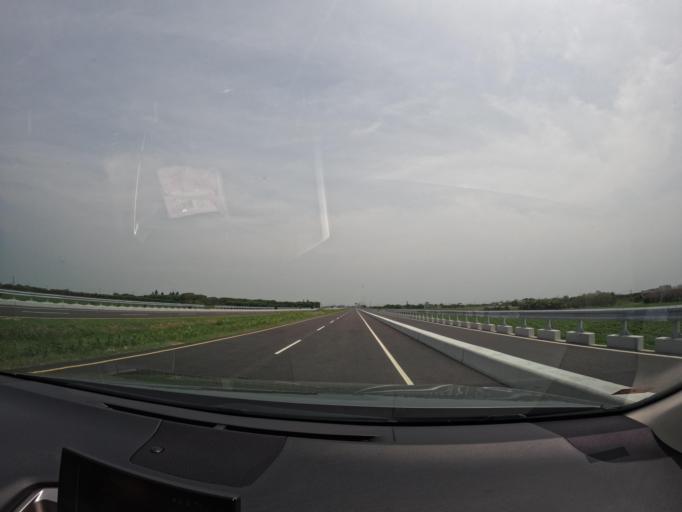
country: TW
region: Taiwan
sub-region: Changhua
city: Chang-hua
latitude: 23.9365
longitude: 120.3401
